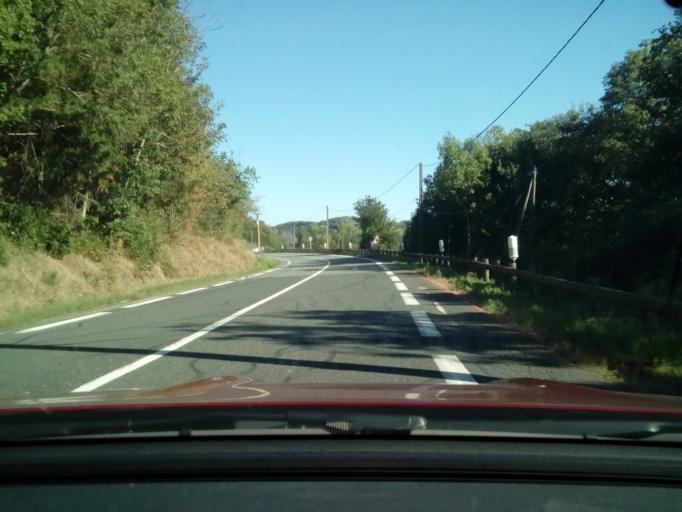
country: FR
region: Rhone-Alpes
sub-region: Departement du Rhone
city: Pontcharra-sur-Turdine
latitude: 45.9192
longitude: 4.4858
